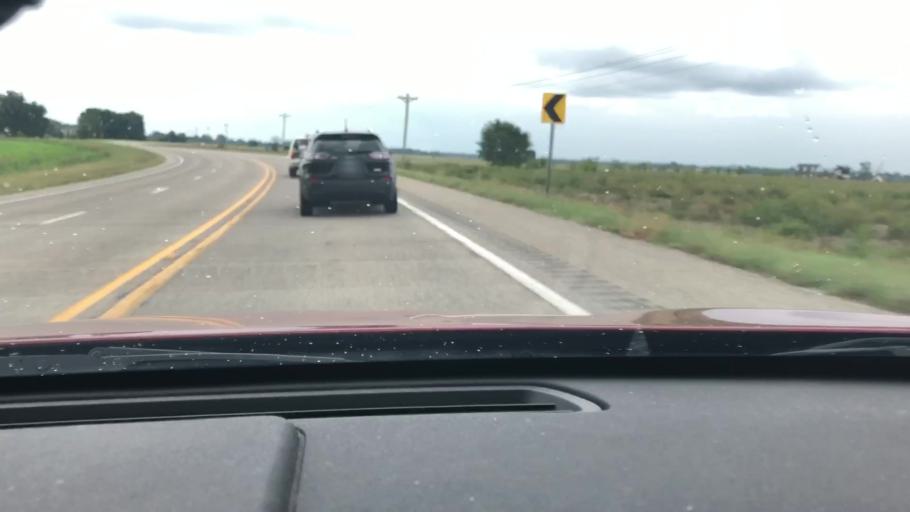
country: US
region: Arkansas
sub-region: Lafayette County
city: Lewisville
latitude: 33.3927
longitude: -93.7394
